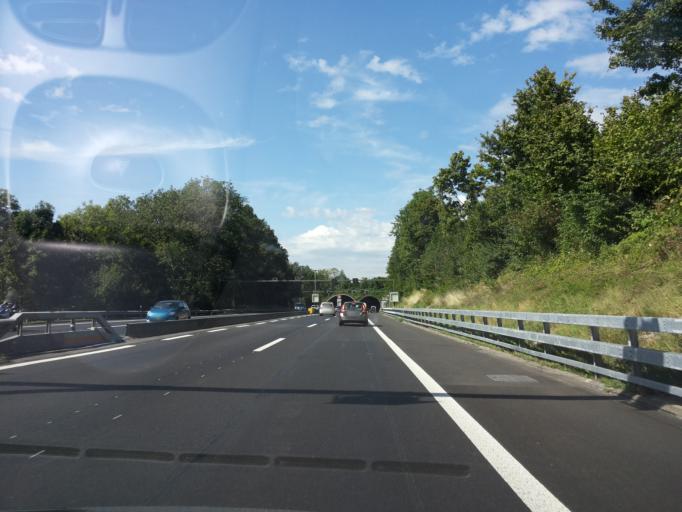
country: CH
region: Lucerne
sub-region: Sursee District
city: Eich
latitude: 47.1473
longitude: 8.1763
